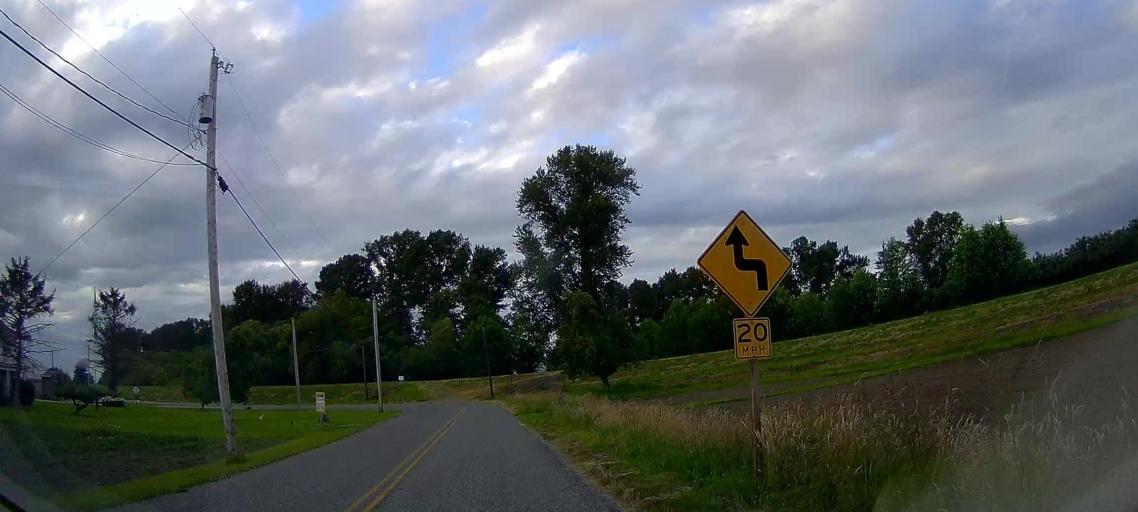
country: US
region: Washington
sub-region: Skagit County
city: Mount Vernon
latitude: 48.3420
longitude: -122.3538
